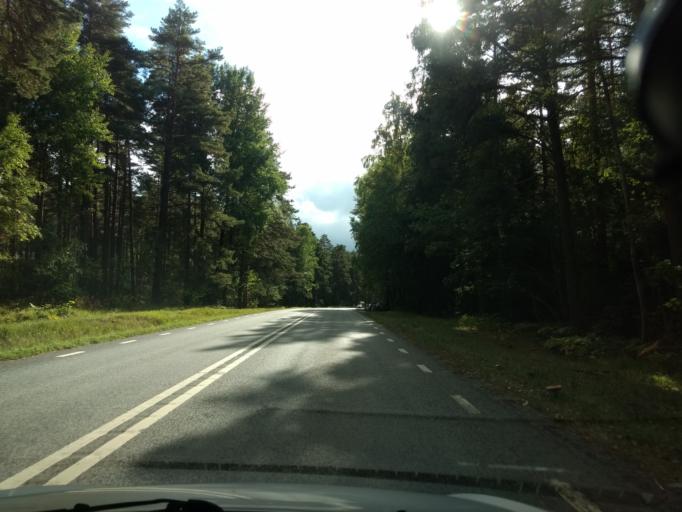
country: SE
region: Uppsala
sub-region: Uppsala Kommun
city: Saevja
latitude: 59.7769
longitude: 17.6627
